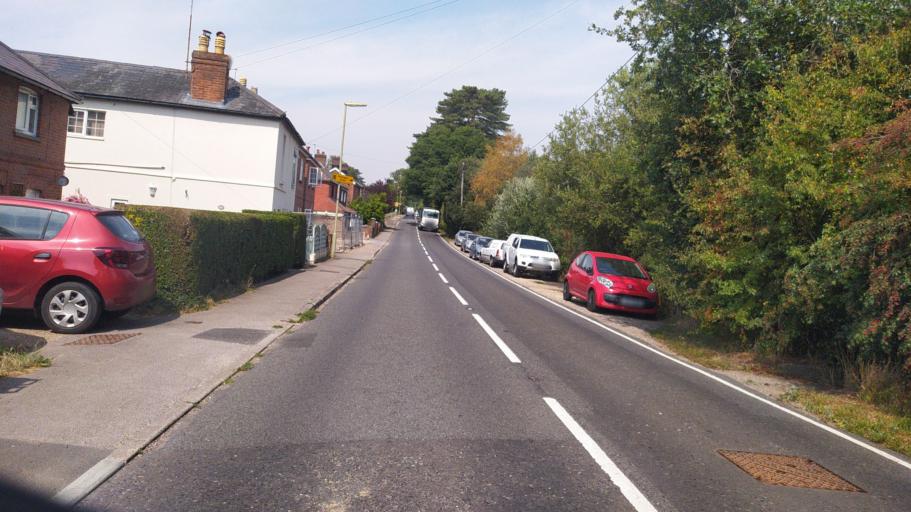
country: GB
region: England
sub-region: Hampshire
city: Havant
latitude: 50.8815
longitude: -0.9647
